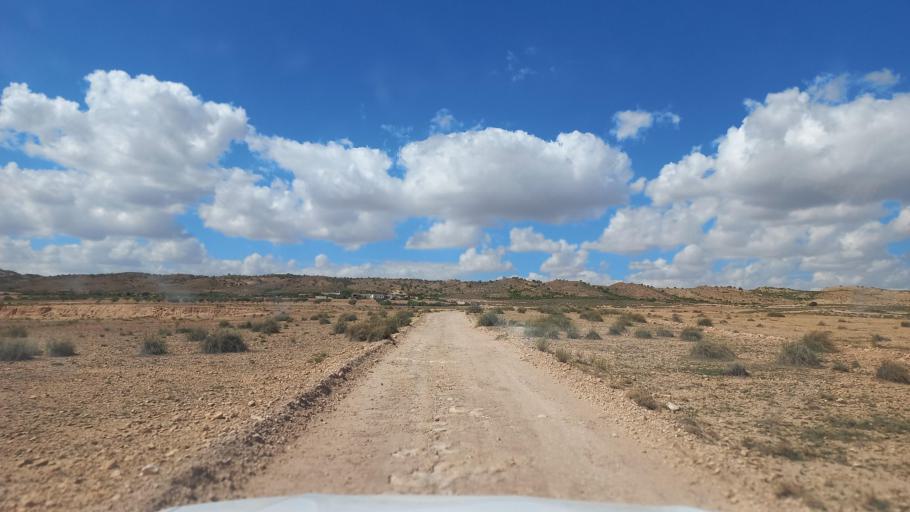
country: TN
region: Al Qasrayn
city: Sbiba
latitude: 35.3616
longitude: 9.0032
